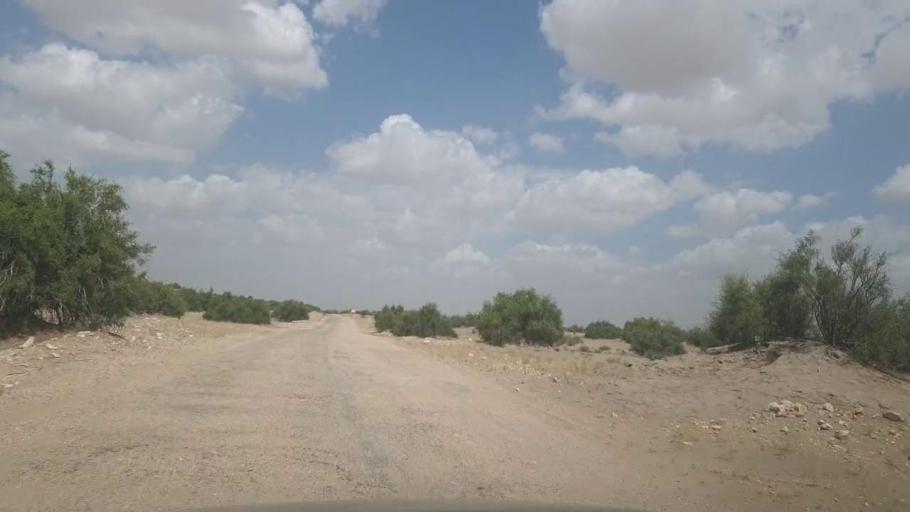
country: PK
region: Sindh
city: Kot Diji
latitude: 27.2676
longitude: 69.1800
